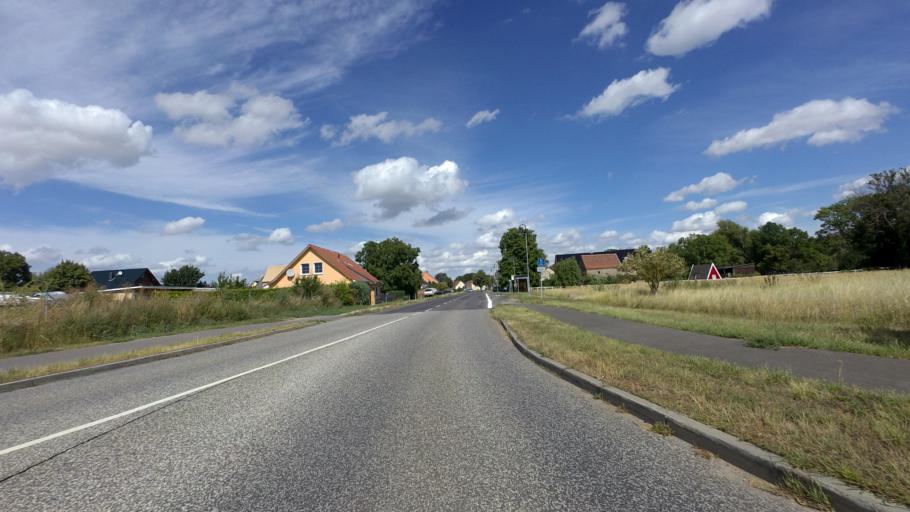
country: DE
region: Brandenburg
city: Wustermark
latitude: 52.5126
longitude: 12.9332
